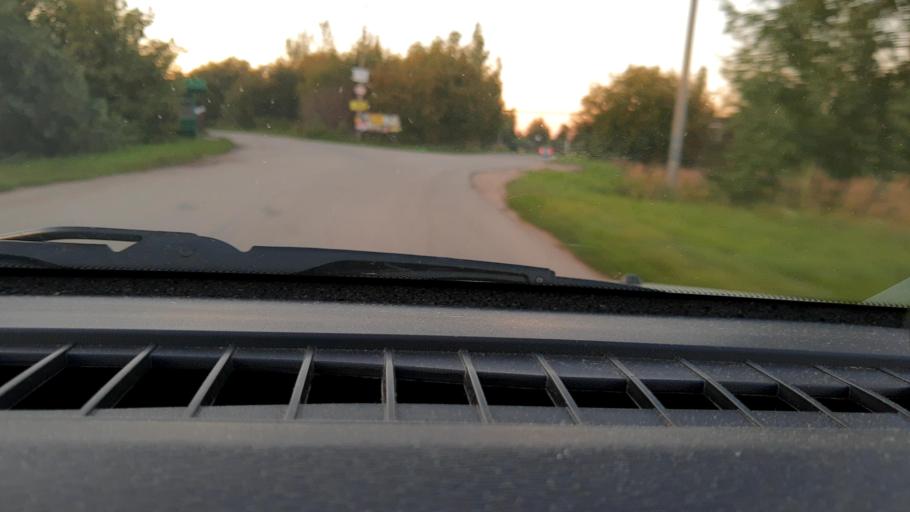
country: RU
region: Nizjnij Novgorod
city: Pamyat' Parizhskoy Kommuny
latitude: 56.0687
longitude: 44.4654
